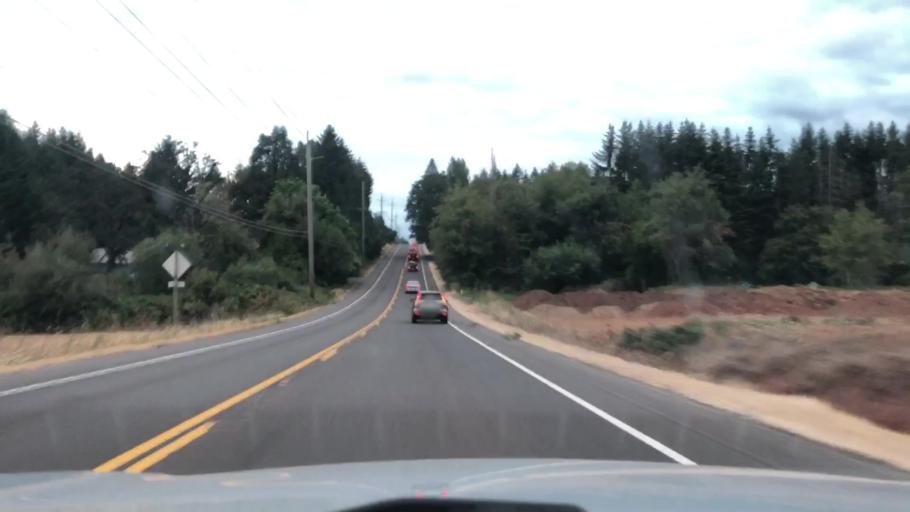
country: US
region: Oregon
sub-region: Clackamas County
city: Beavercreek
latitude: 45.2730
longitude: -122.5696
